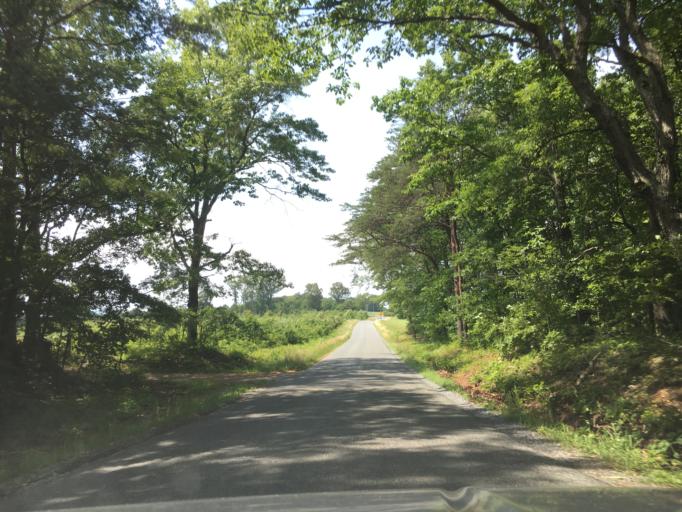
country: US
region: Virginia
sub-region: Pittsylvania County
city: Chatham
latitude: 36.8874
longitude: -79.4055
